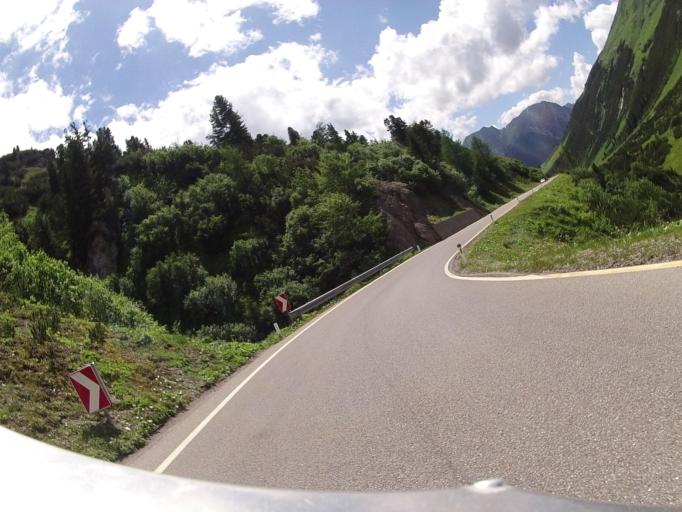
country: AT
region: Tyrol
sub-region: Politischer Bezirk Reutte
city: Namlos
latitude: 47.2867
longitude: 10.6484
